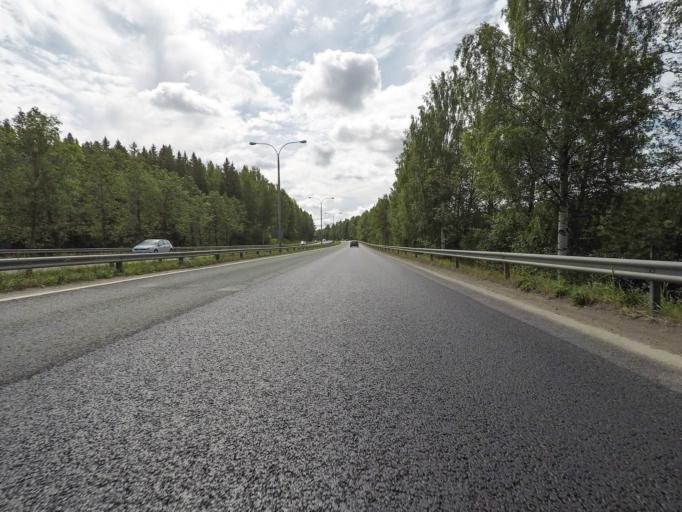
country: FI
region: Northern Savo
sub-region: Kuopio
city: Kuopio
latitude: 62.9268
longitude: 27.6753
